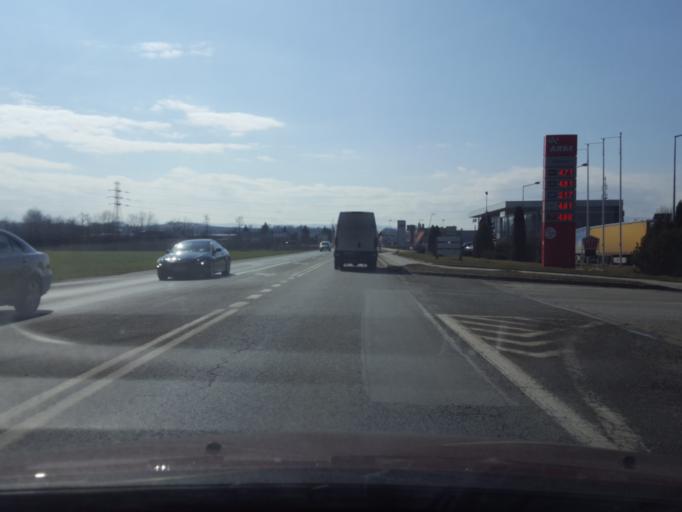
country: PL
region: Lesser Poland Voivodeship
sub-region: Powiat nowosadecki
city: Chelmiec
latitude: 49.6598
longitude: 20.6893
